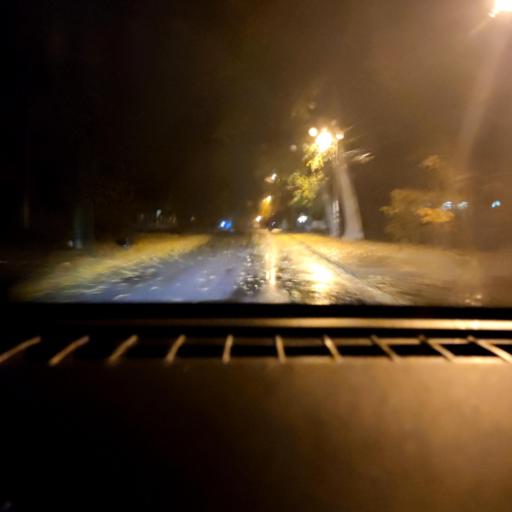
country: RU
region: Voronezj
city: Somovo
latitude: 51.7376
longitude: 39.3669
